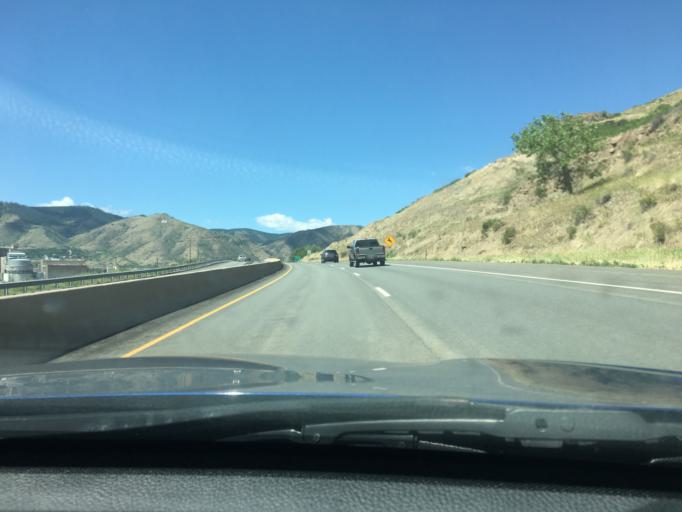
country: US
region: Colorado
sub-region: Jefferson County
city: Golden
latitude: 39.7691
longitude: -105.2046
